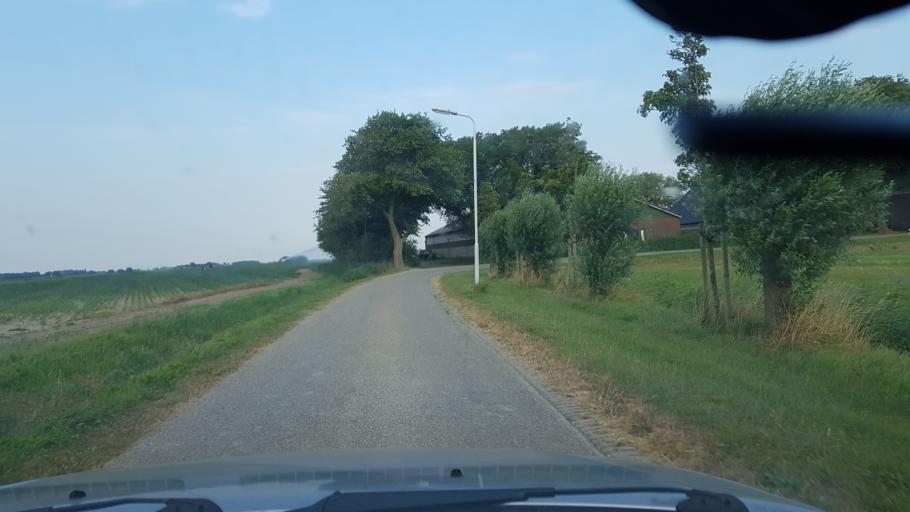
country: NL
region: Friesland
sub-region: Gemeente Dongeradeel
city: Holwerd
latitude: 53.3480
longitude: 5.8775
